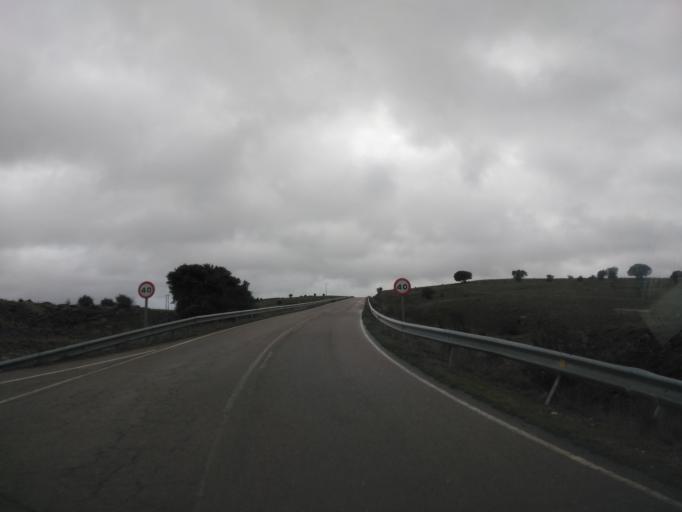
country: ES
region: Castille and Leon
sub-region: Provincia de Salamanca
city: Doninos de Salamanca
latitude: 40.9708
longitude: -5.7140
